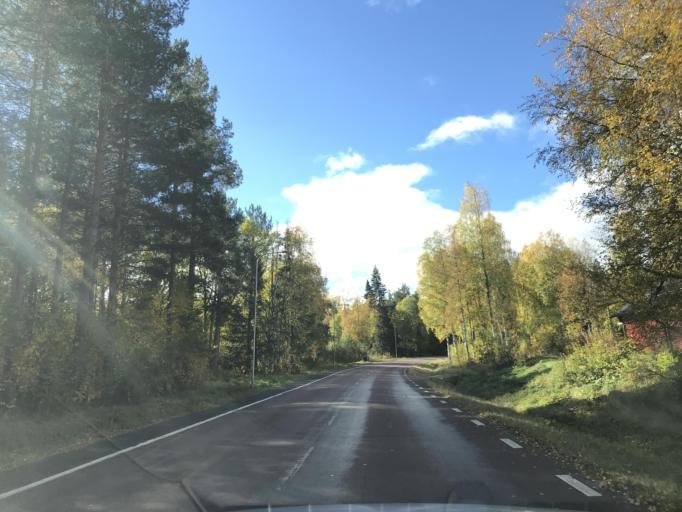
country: NO
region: Hedmark
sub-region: Trysil
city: Innbygda
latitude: 61.6891
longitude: 13.1376
